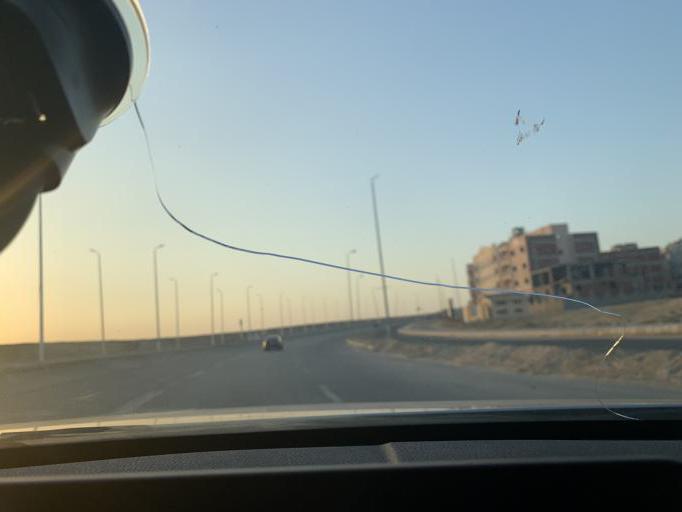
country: EG
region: Muhafazat al Qahirah
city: Halwan
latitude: 29.9768
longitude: 31.4700
